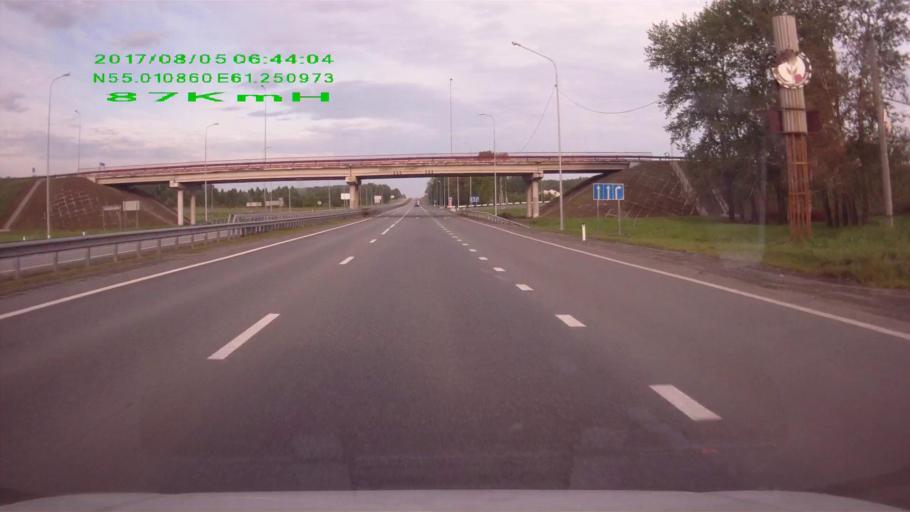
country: RU
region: Chelyabinsk
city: Sargazy
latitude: 55.0108
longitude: 61.2504
